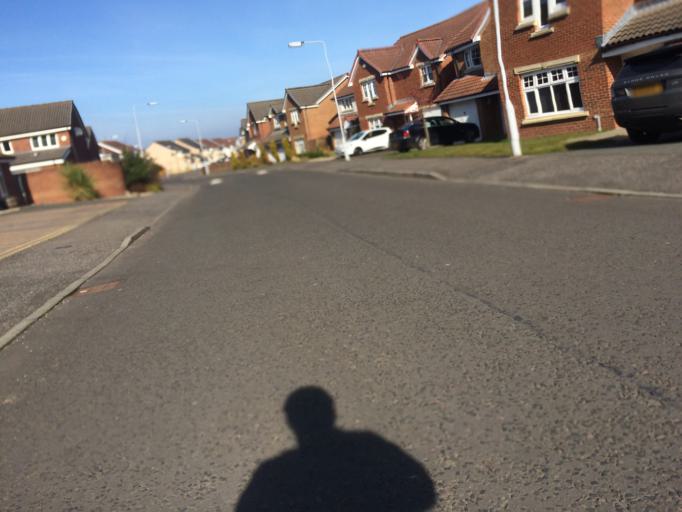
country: GB
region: Scotland
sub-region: Fife
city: Kirkcaldy
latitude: 56.1372
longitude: -3.1905
